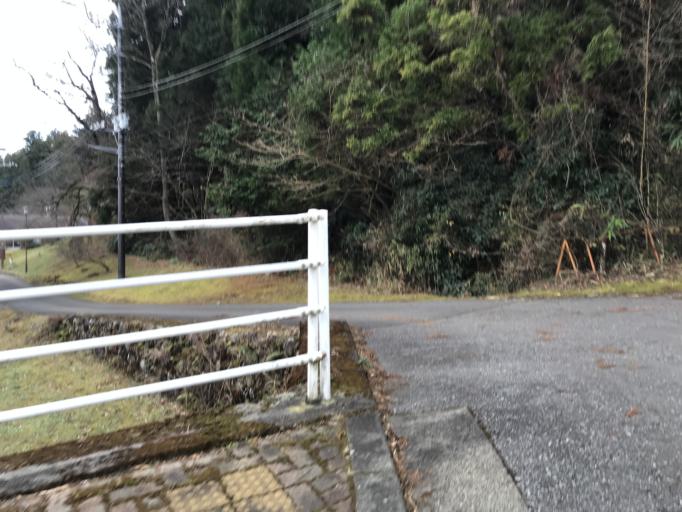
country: JP
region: Tochigi
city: Imaichi
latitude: 36.7299
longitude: 139.6725
